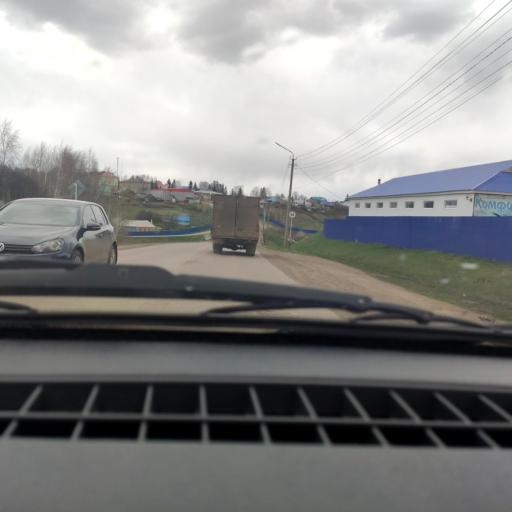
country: RU
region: Bashkortostan
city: Chekmagush
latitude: 55.1332
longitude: 54.6544
